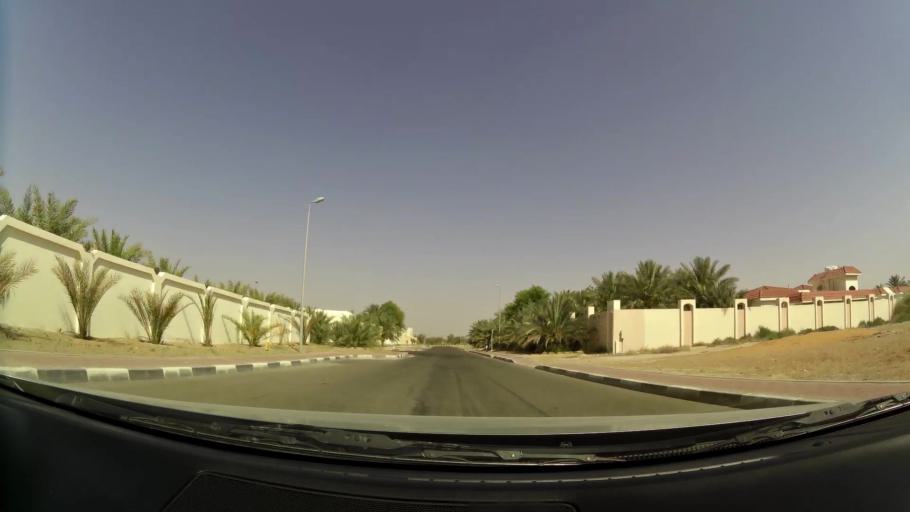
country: OM
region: Al Buraimi
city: Al Buraymi
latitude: 24.3070
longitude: 55.7976
